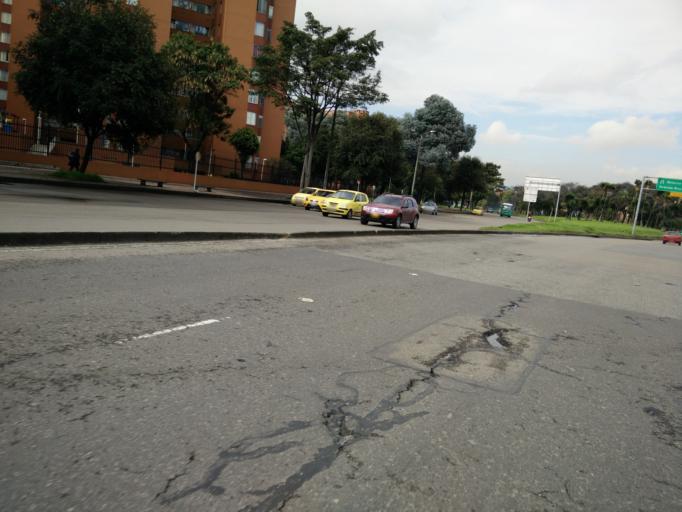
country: CO
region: Bogota D.C.
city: Bogota
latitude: 4.6619
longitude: -74.1108
